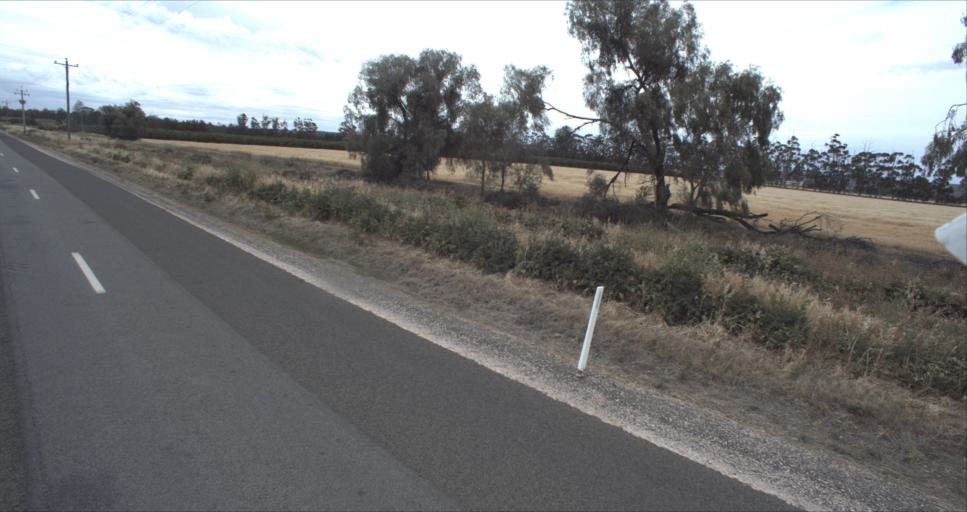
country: AU
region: New South Wales
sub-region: Leeton
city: Leeton
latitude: -34.4697
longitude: 146.3957
